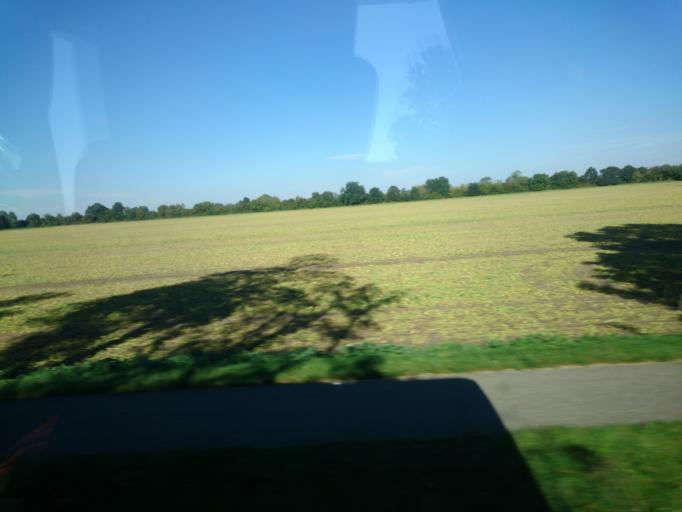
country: DE
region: Mecklenburg-Vorpommern
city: Ducherow
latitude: 53.7696
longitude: 13.7730
